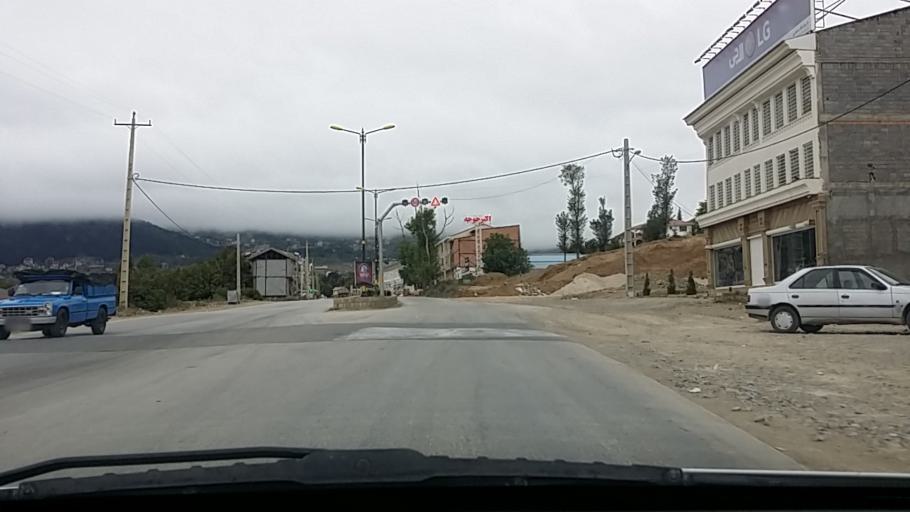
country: IR
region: Mazandaran
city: `Abbasabad
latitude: 36.5130
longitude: 51.1597
